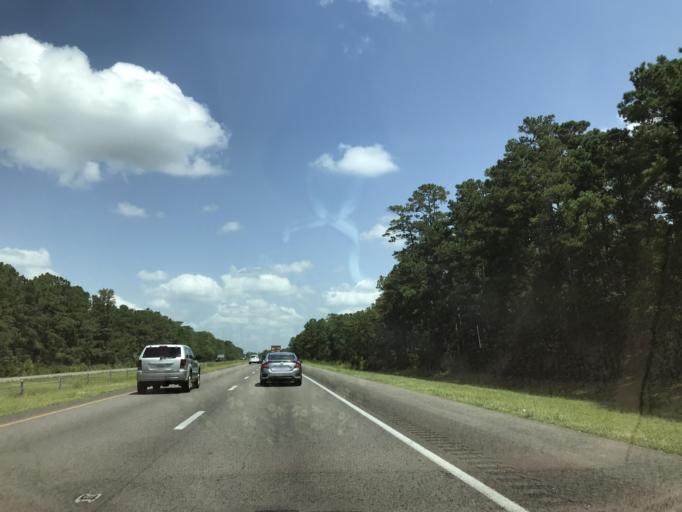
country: US
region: North Carolina
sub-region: New Hanover County
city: Castle Hayne
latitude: 34.3799
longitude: -77.8816
